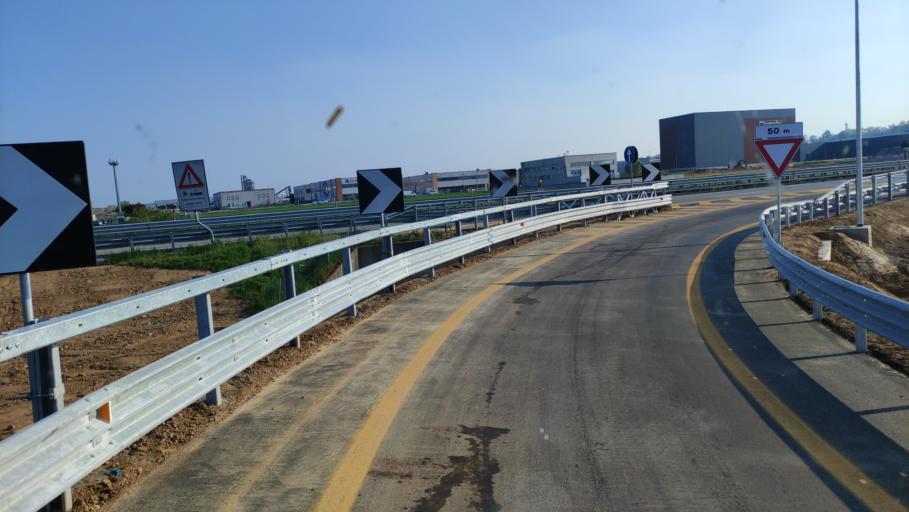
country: IT
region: Piedmont
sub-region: Provincia di Cuneo
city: Cervere
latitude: 44.6634
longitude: 7.7828
